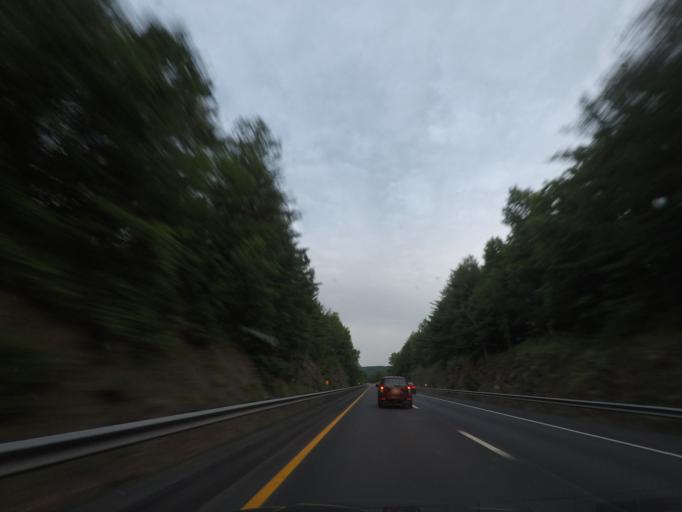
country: US
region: New York
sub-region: Rensselaer County
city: Nassau
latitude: 42.4503
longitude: -73.5732
